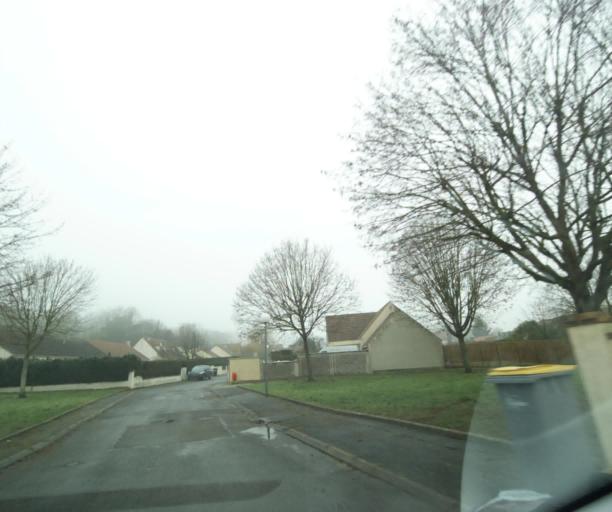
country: FR
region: Ile-de-France
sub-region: Departement de Seine-et-Marne
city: Dammartin-en-Goele
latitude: 49.0598
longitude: 2.6796
